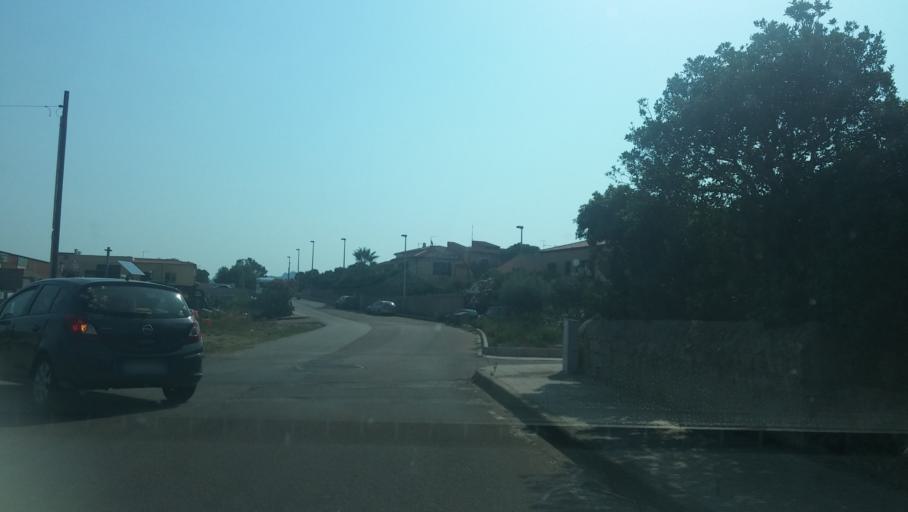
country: IT
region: Sardinia
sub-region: Provincia di Olbia-Tempio
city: La Maddalena
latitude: 41.2218
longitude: 9.4332
